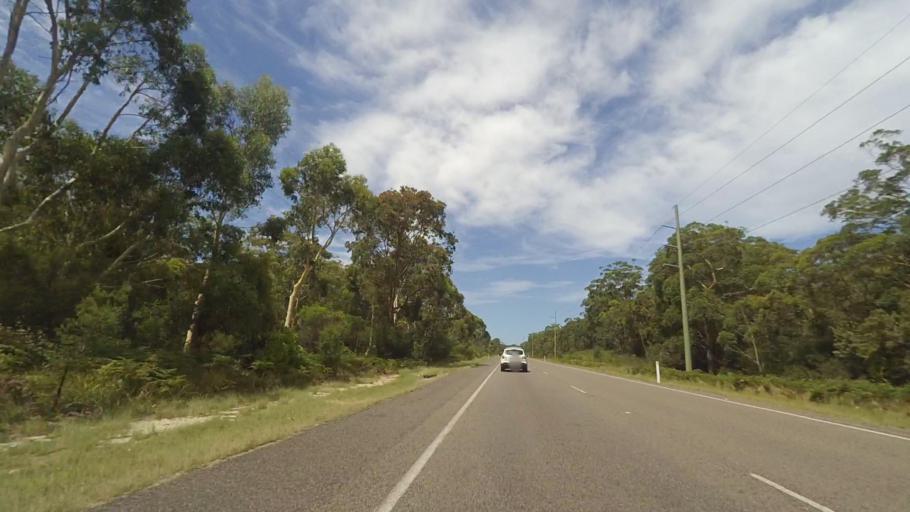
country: AU
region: New South Wales
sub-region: Port Stephens Shire
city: Medowie
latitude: -32.7902
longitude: 151.9578
